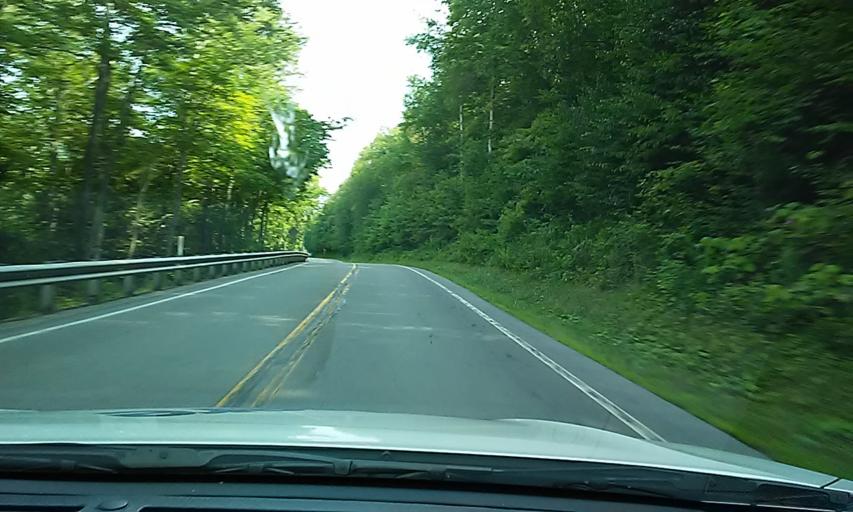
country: US
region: Pennsylvania
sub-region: Potter County
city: Galeton
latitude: 41.7994
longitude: -77.7716
